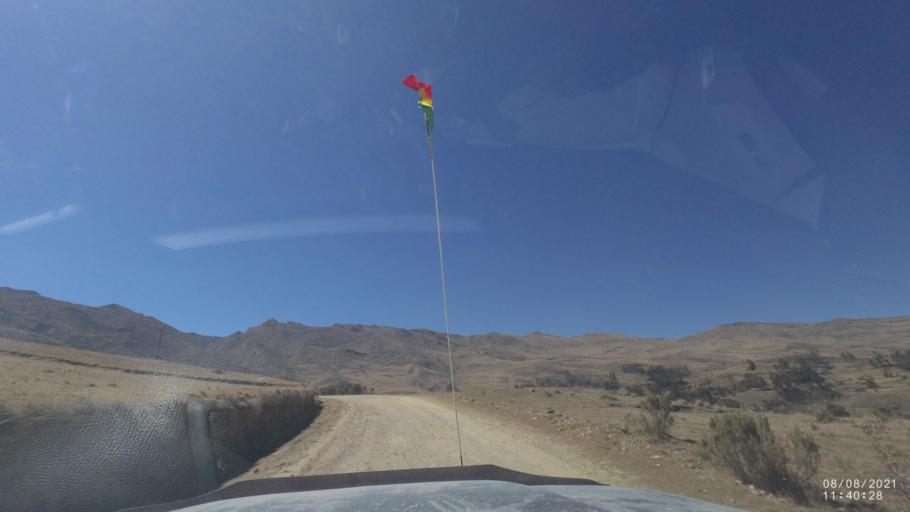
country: BO
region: Cochabamba
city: Colchani
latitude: -16.7969
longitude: -66.6479
